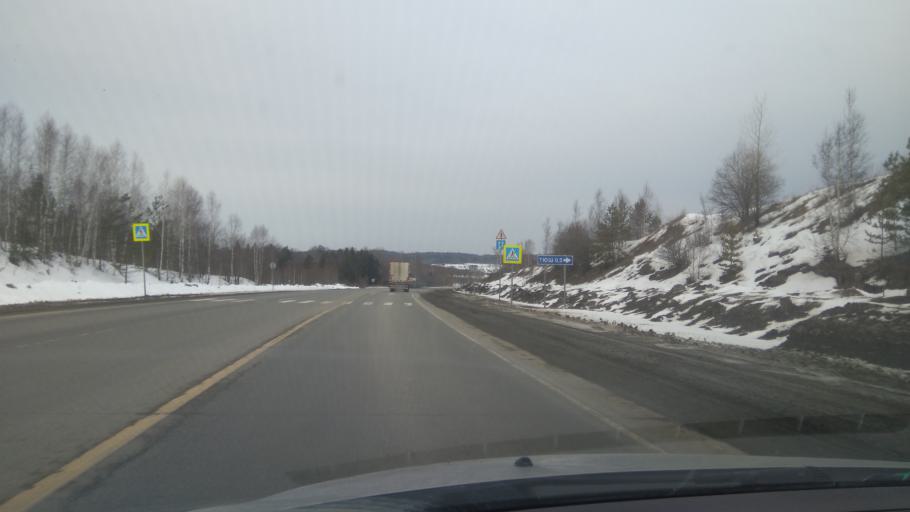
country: RU
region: Sverdlovsk
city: Ufimskiy
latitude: 56.7867
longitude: 58.3668
